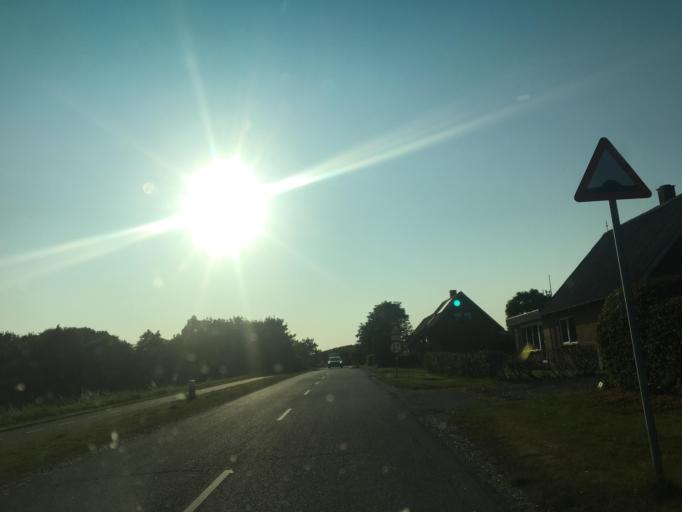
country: DK
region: North Denmark
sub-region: Thisted Kommune
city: Hurup
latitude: 56.8157
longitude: 8.3881
